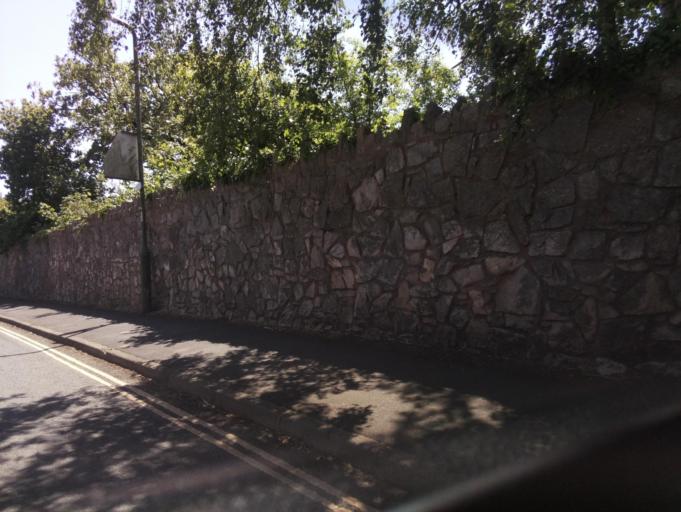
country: GB
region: England
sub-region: Borough of Torbay
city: Paignton
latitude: 50.4291
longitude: -3.5818
